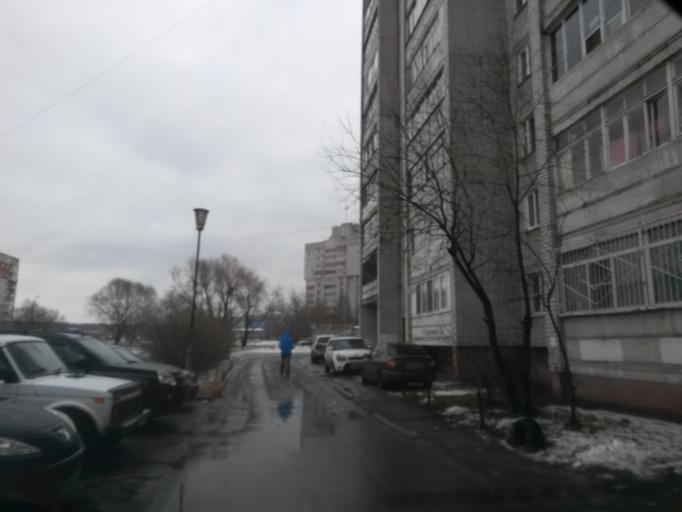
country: RU
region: Jaroslavl
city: Yaroslavl
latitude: 57.6522
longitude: 39.9597
